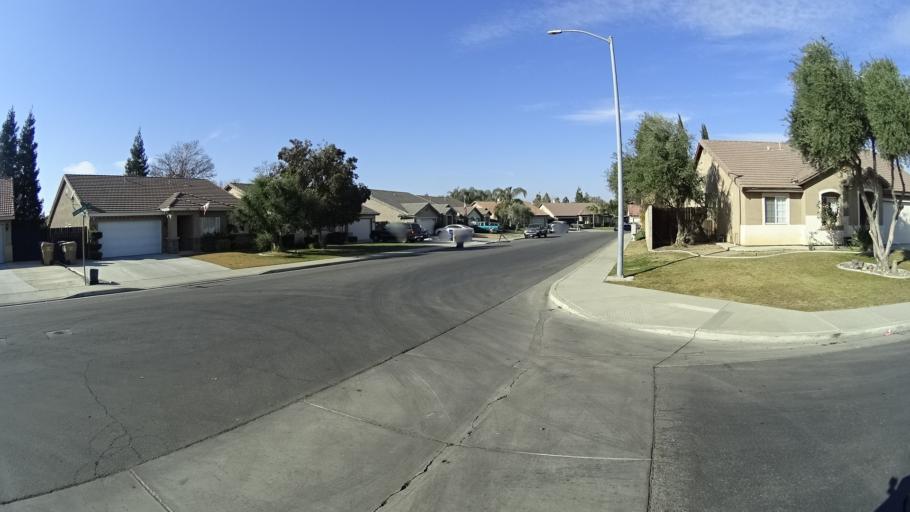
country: US
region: California
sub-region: Kern County
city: Greenacres
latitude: 35.3995
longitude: -119.0958
